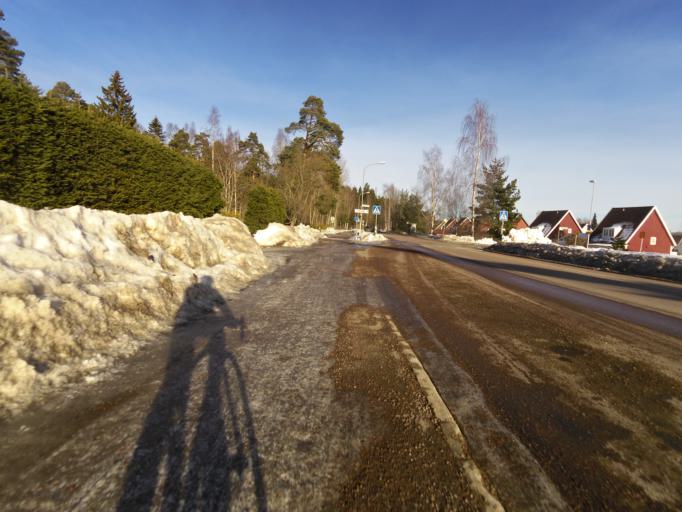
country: SE
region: Gaevleborg
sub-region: Gavle Kommun
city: Valbo
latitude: 60.6613
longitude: 17.0584
